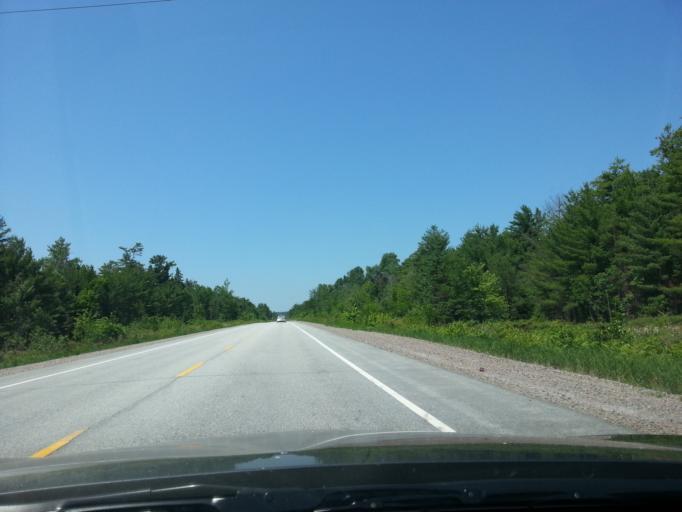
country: CA
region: Ontario
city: Arnprior
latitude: 45.5279
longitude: -76.2107
